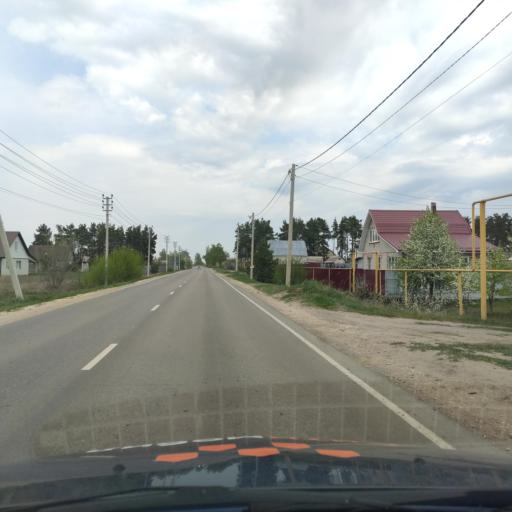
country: RU
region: Voronezj
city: Podgornoye
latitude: 51.8744
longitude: 39.1731
